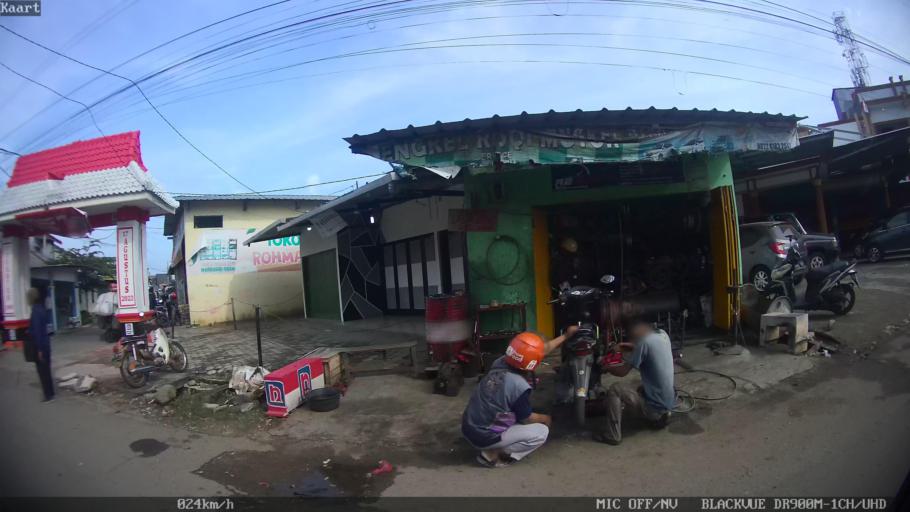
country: ID
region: Lampung
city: Kedaton
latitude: -5.3840
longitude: 105.2715
